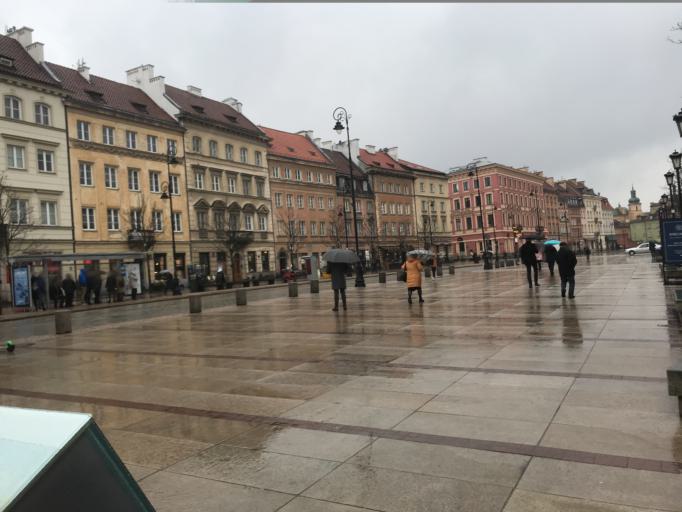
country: PL
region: Masovian Voivodeship
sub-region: Warszawa
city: Warsaw
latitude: 52.2452
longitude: 21.0141
